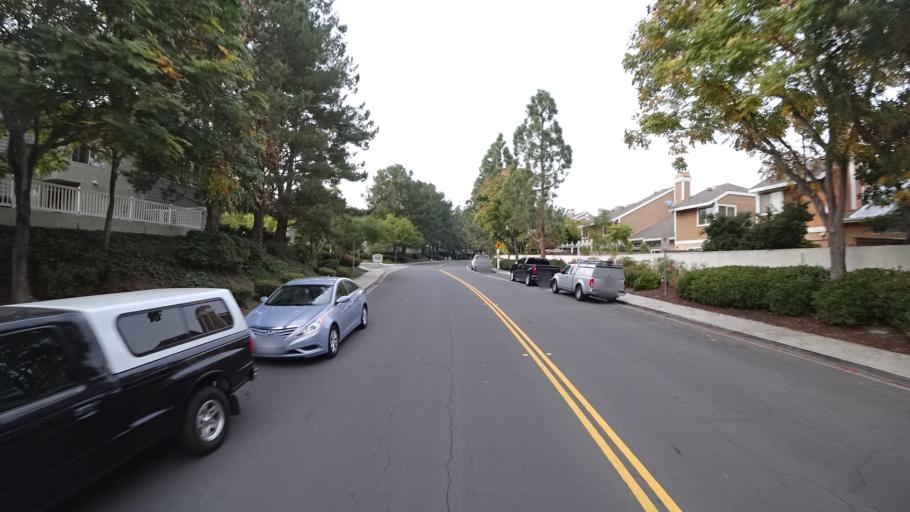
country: US
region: California
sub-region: Orange County
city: Laguna Woods
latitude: 33.5907
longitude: -117.7201
